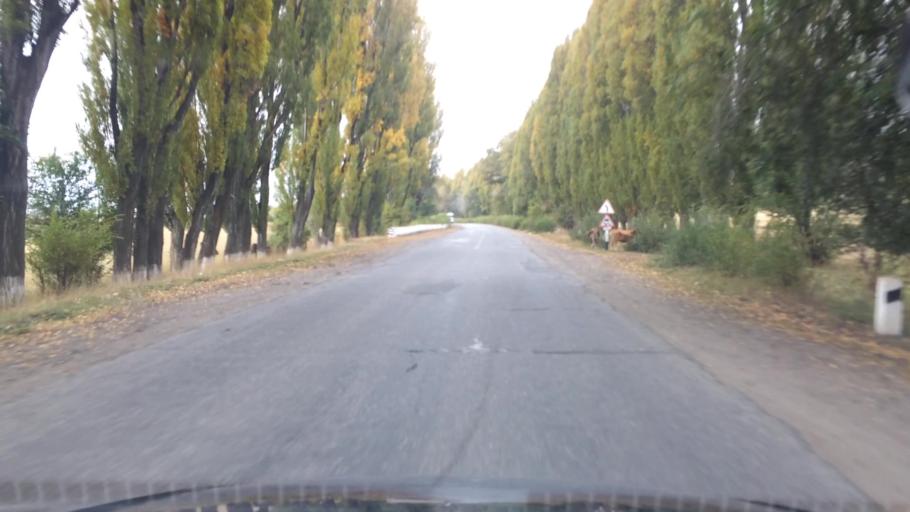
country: KG
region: Ysyk-Koel
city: Pokrovka
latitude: 42.7393
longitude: 77.9080
